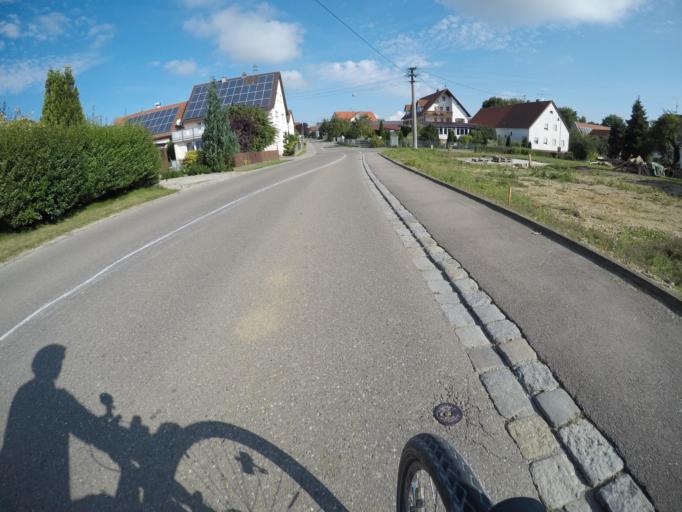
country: DE
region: Bavaria
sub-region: Swabia
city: Allmannshofen
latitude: 48.6124
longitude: 10.8045
